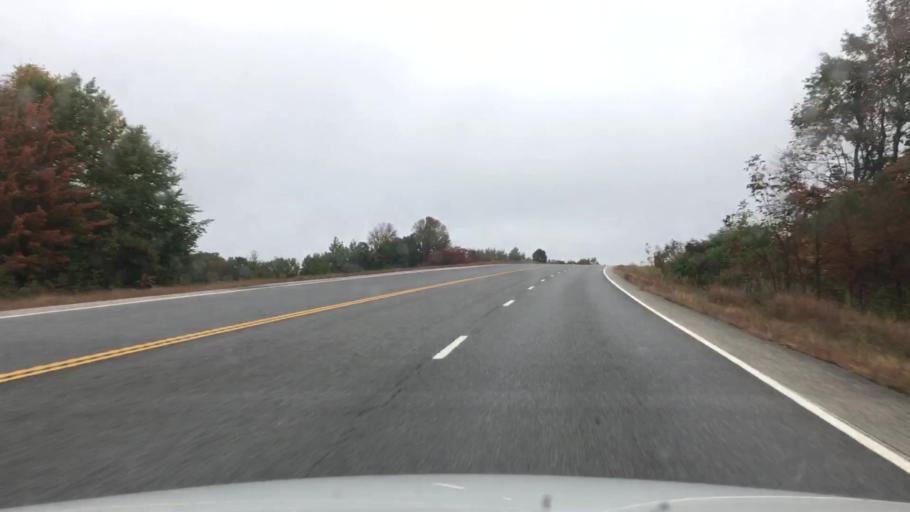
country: US
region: Maine
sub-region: Androscoggin County
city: Poland
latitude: 43.9814
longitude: -70.3679
